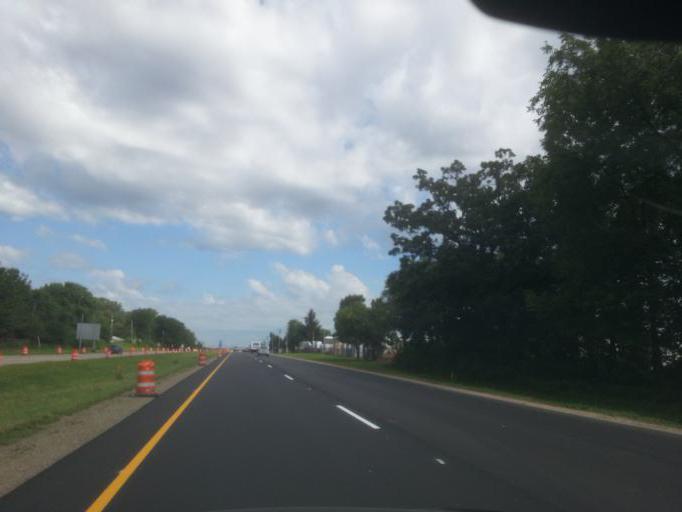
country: US
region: Wisconsin
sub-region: Dane County
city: Monona
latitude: 43.0902
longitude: -89.3136
